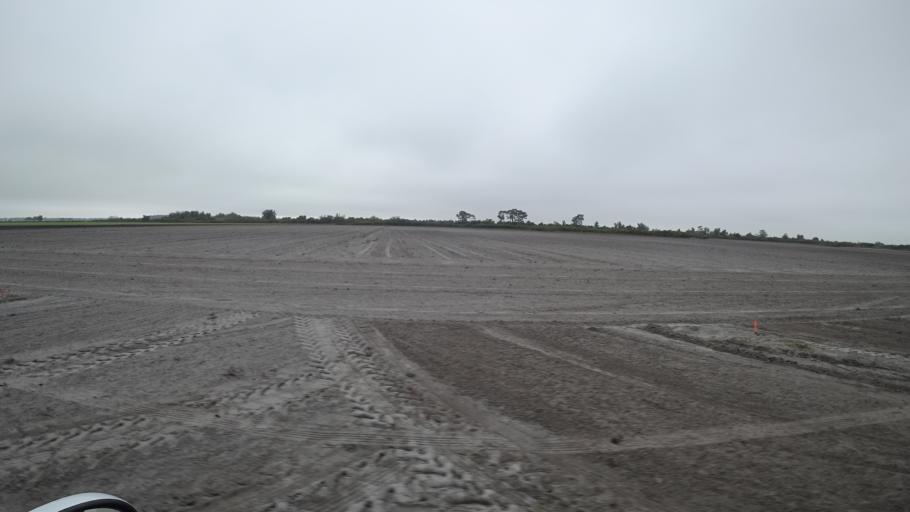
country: US
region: Florida
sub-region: Sarasota County
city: Warm Mineral Springs
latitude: 27.2991
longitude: -82.1680
